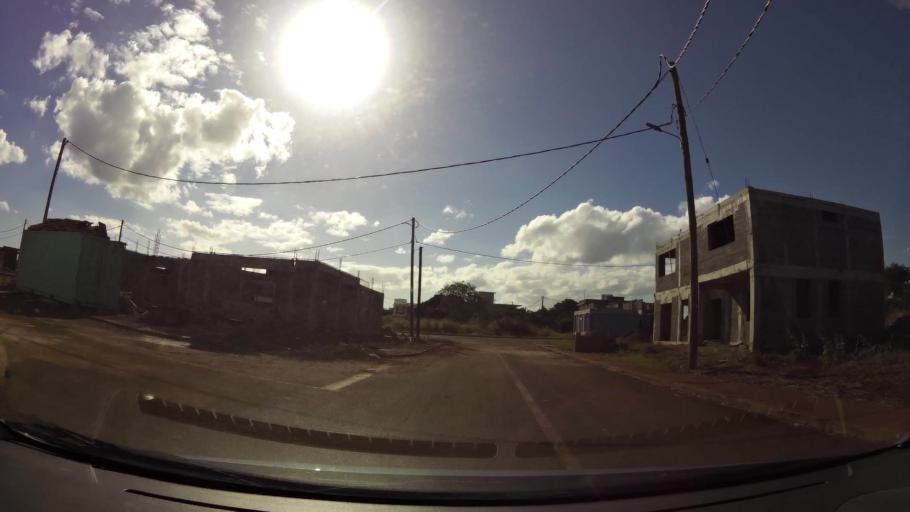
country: MU
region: Black River
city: Albion
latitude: -20.2009
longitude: 57.4134
